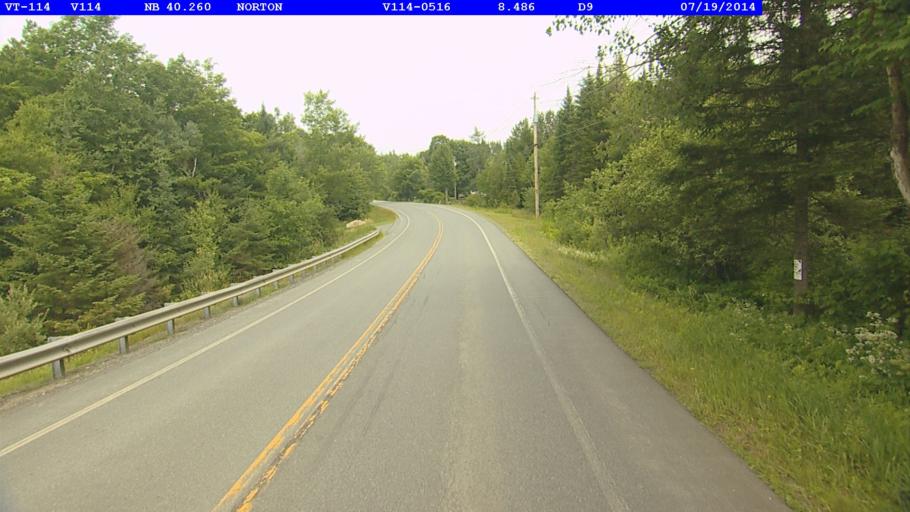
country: CA
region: Quebec
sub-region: Estrie
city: Coaticook
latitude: 44.9959
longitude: -71.7359
